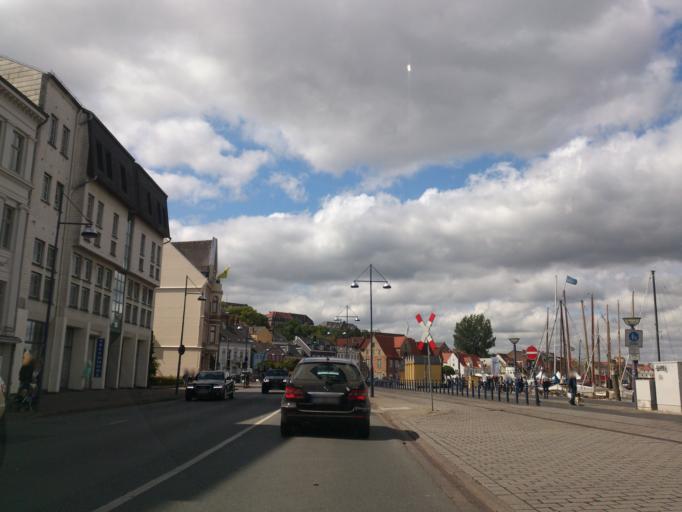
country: DE
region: Schleswig-Holstein
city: Flensburg
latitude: 54.7885
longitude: 9.4356
